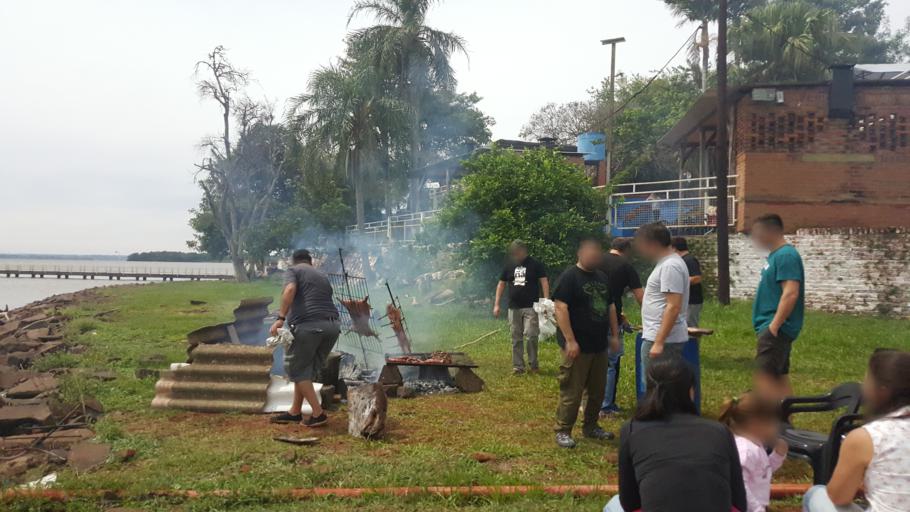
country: PY
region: Itapua
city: San Juan del Parana
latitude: -27.3598
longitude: -55.9570
